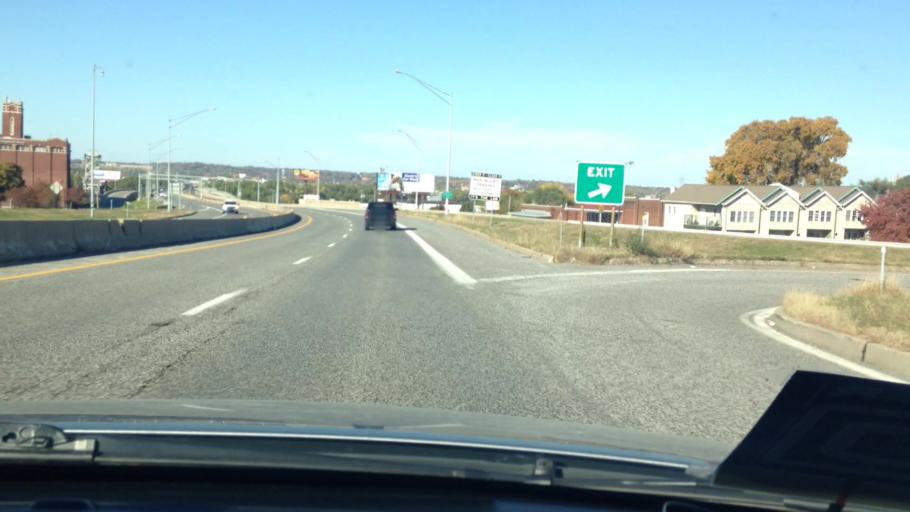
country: US
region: Missouri
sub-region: Jackson County
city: Kansas City
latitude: 39.1077
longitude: -94.5769
